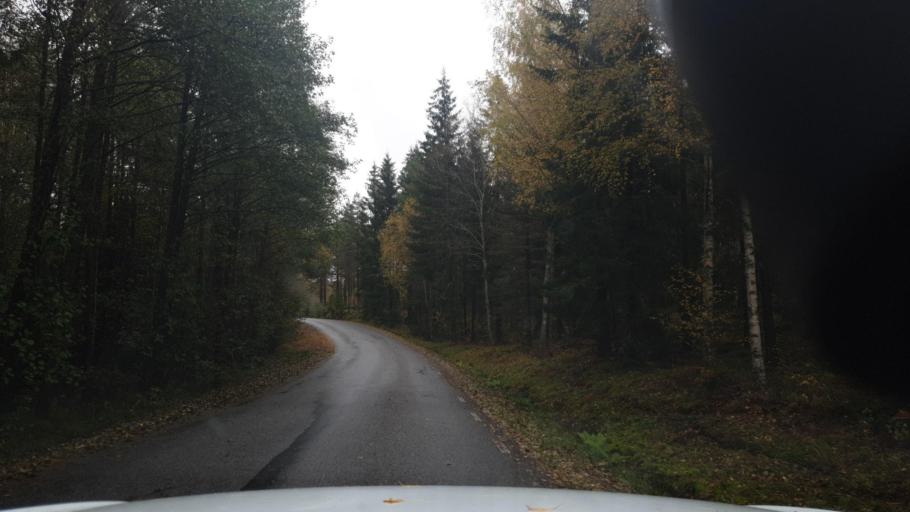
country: SE
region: Vaermland
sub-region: Karlstads Kommun
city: Valberg
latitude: 59.4166
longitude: 13.1460
